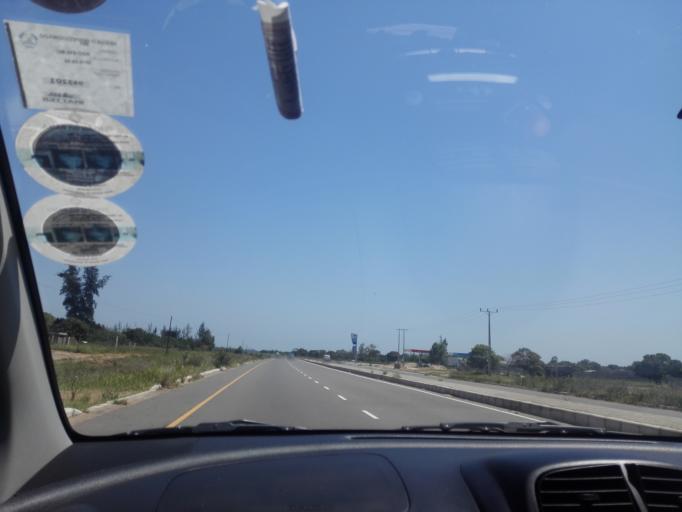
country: MZ
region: Maputo City
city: Maputo
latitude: -25.8063
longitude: 32.6727
